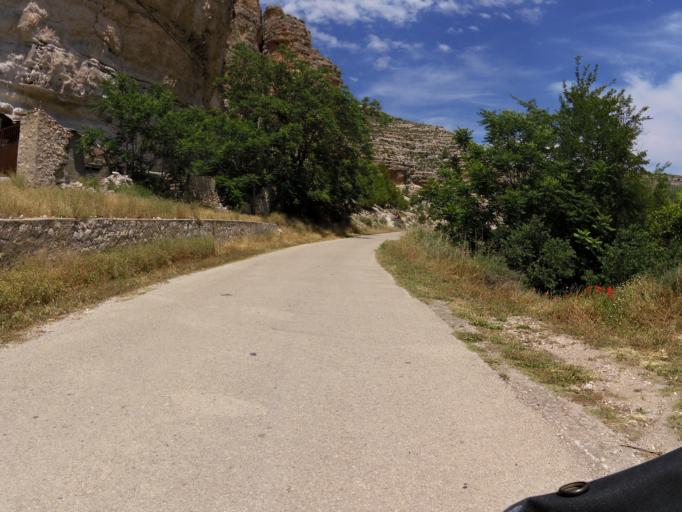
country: ES
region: Castille-La Mancha
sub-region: Provincia de Albacete
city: Jorquera
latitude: 39.1679
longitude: -1.5612
